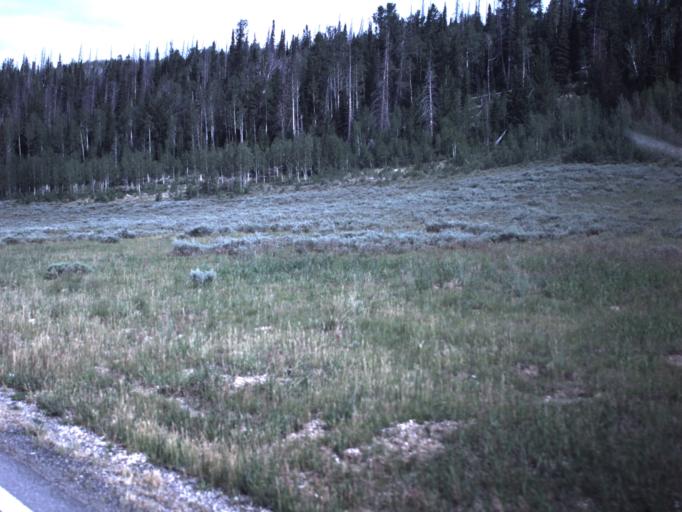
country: US
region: Utah
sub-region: Iron County
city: Parowan
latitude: 37.5706
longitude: -112.8063
